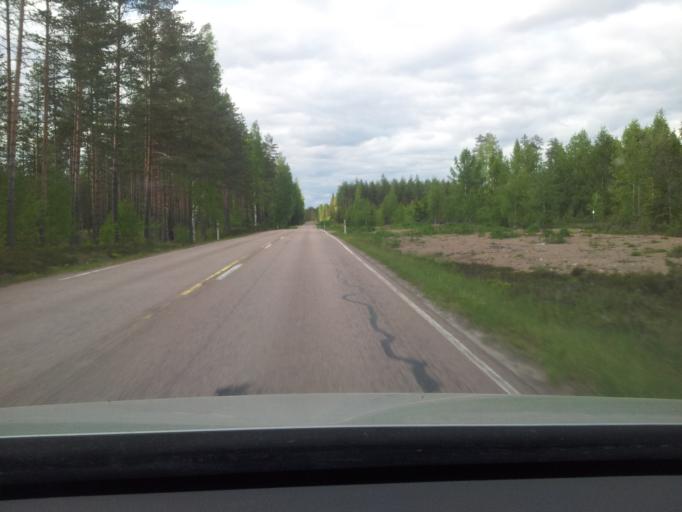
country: FI
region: South Karelia
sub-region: Lappeenranta
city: Luumaeki
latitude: 60.9385
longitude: 27.5834
